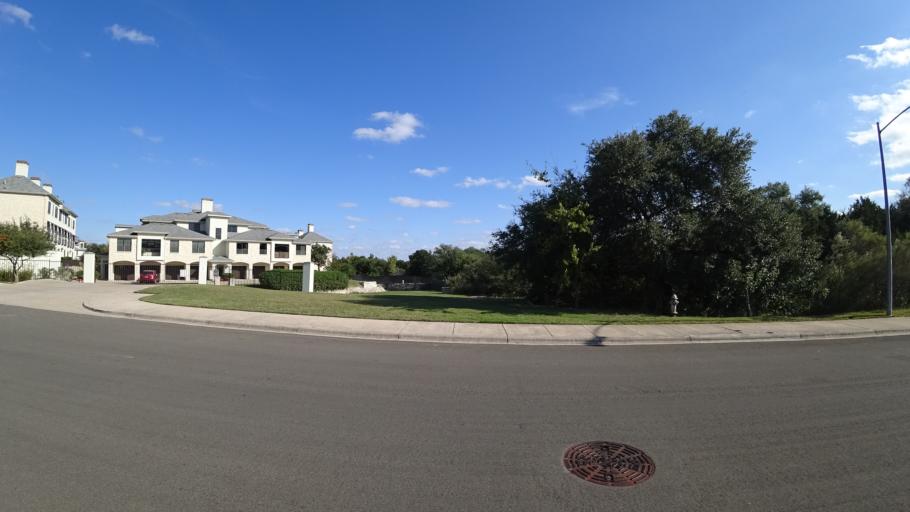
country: US
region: Texas
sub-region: Travis County
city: Barton Creek
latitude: 30.2523
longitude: -97.8774
